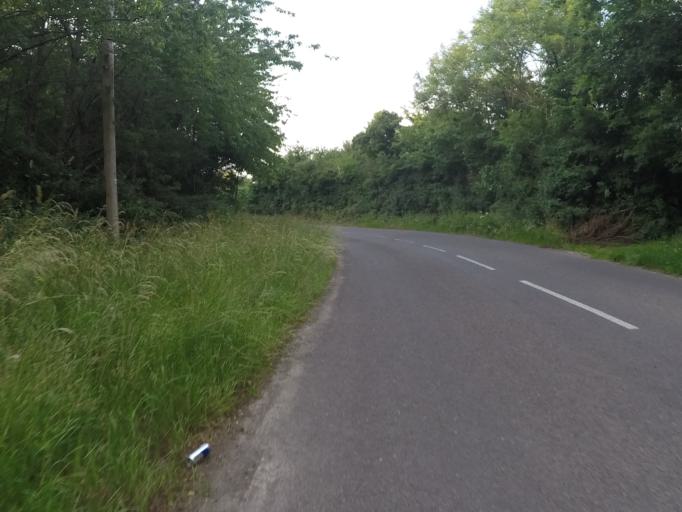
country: GB
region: England
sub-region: Oxfordshire
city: Charlbury
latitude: 51.8794
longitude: -1.4866
